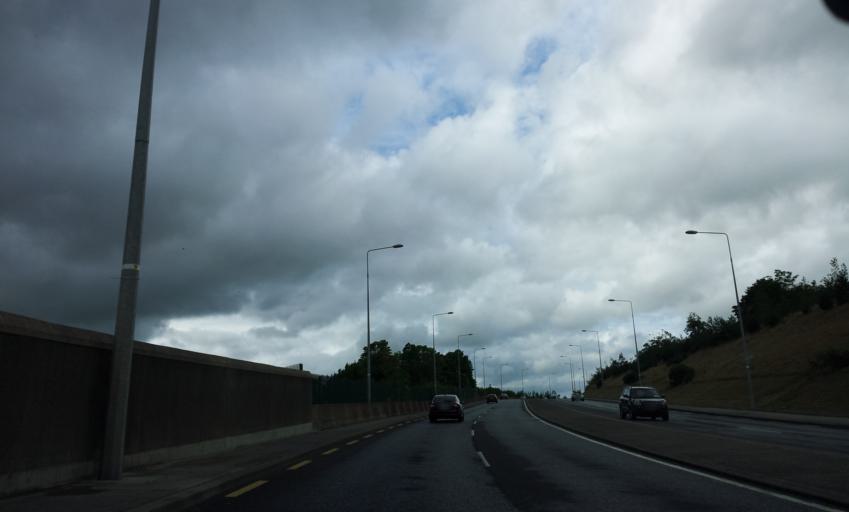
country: IE
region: Munster
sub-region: Waterford
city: Waterford
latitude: 52.2689
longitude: -7.1303
